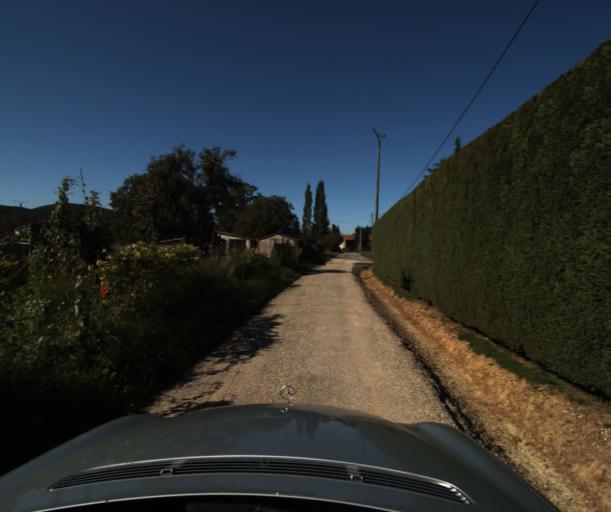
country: FR
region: Midi-Pyrenees
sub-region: Departement de l'Ariege
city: Lavelanet
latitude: 42.9848
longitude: 1.9114
